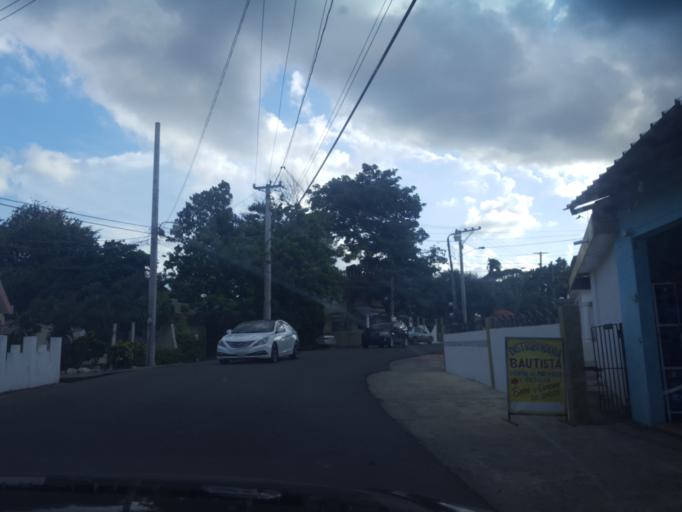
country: DO
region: Santiago
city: Licey al Medio
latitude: 19.3738
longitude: -70.6363
